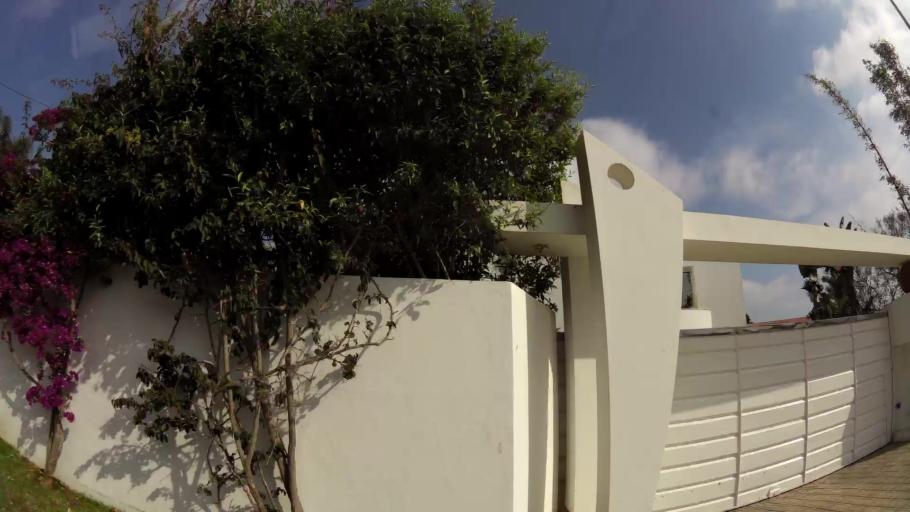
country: MA
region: Rabat-Sale-Zemmour-Zaer
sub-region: Rabat
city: Rabat
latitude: 33.9688
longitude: -6.8428
